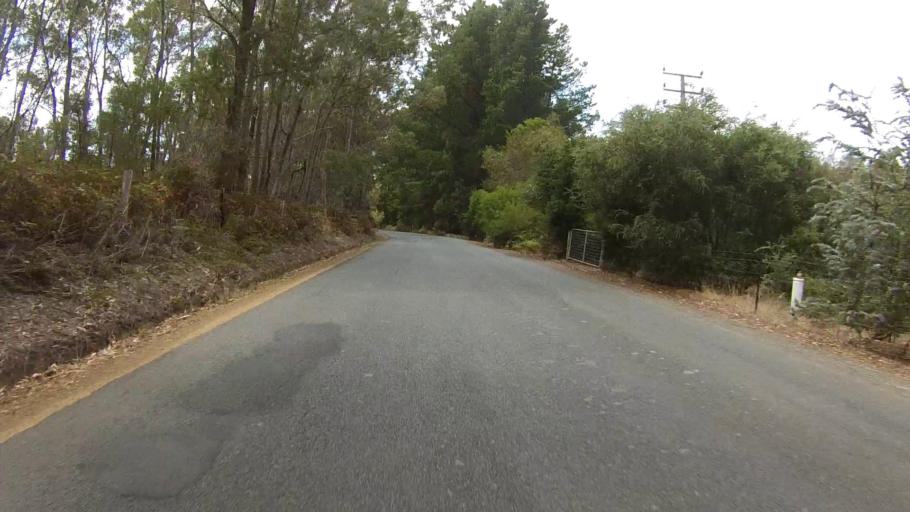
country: AU
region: Tasmania
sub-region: Kingborough
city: Margate
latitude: -43.0094
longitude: 147.2815
